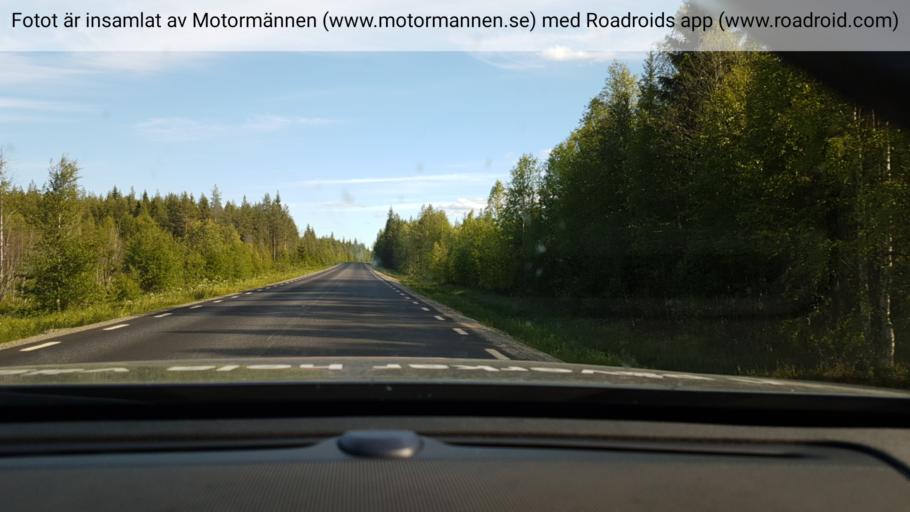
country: SE
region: Vaesterbotten
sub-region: Vindelns Kommun
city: Vindeln
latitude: 64.4174
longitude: 19.3643
